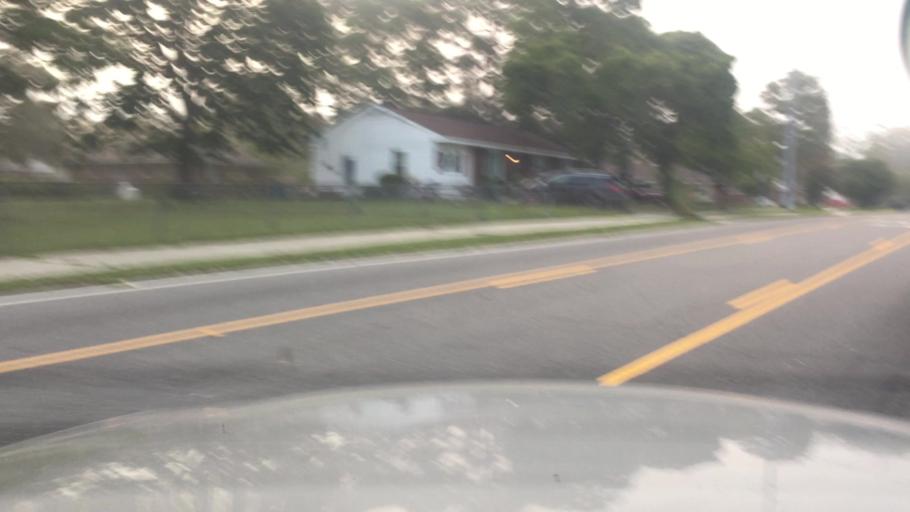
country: US
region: North Carolina
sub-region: Cumberland County
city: Hope Mills
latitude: 35.0240
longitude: -78.9417
